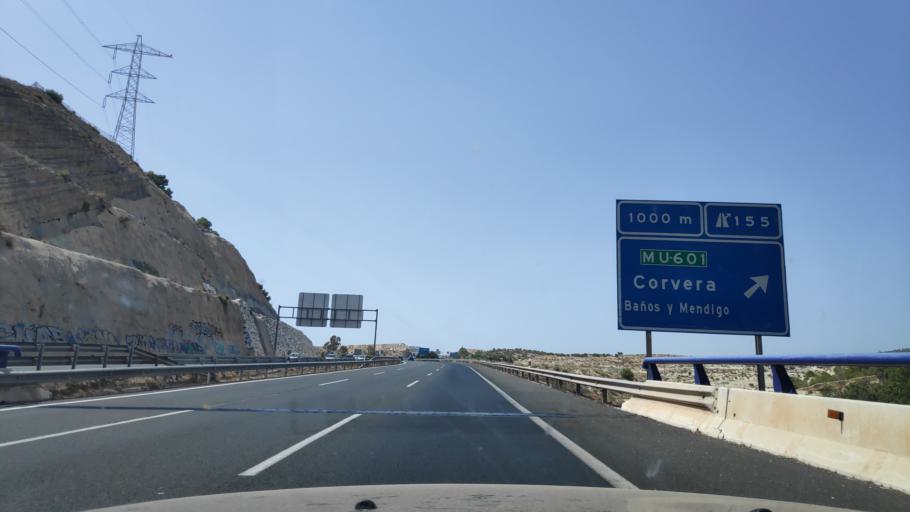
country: ES
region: Murcia
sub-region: Murcia
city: Murcia
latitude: 37.8734
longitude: -1.1267
